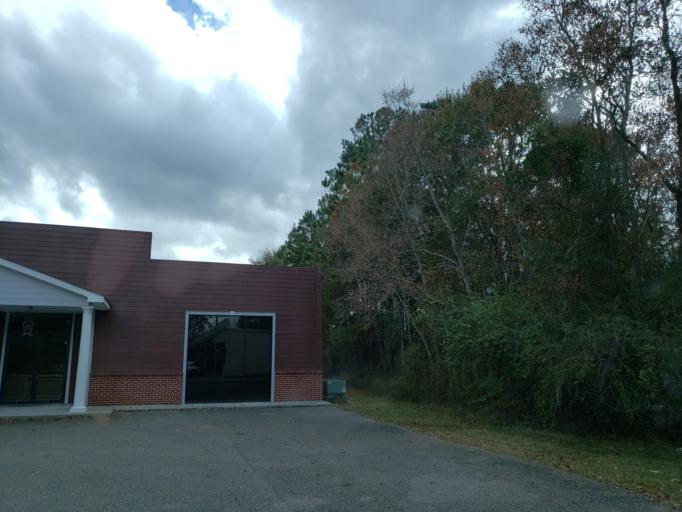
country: US
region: Mississippi
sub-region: Lamar County
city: West Hattiesburg
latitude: 31.3173
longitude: -89.3617
